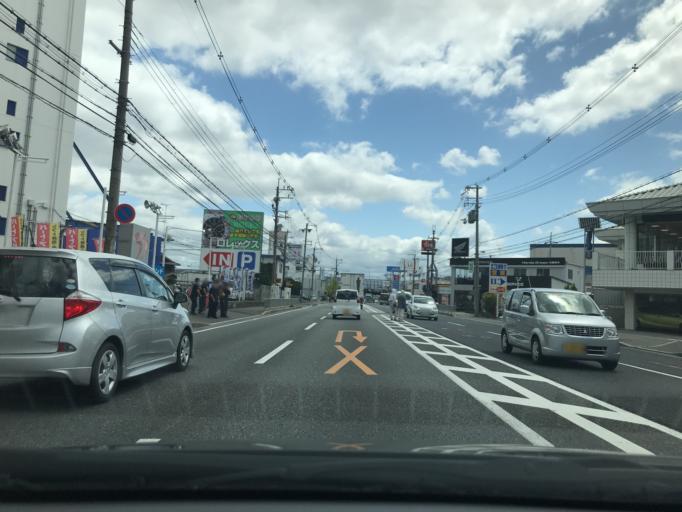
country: JP
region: Osaka
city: Ibaraki
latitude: 34.8338
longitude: 135.5575
